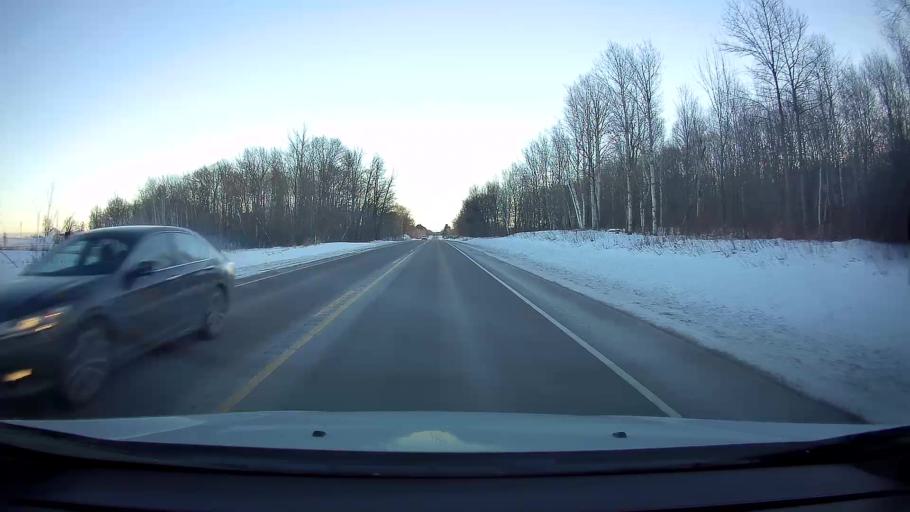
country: US
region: Wisconsin
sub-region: Washburn County
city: Shell Lake
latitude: 45.6867
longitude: -91.9761
